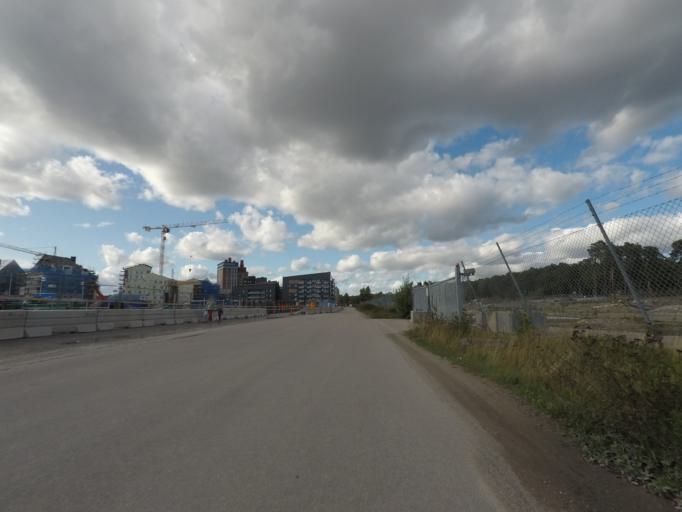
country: SE
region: Vaestmanland
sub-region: Vasteras
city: Vasteras
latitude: 59.6050
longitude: 16.5753
